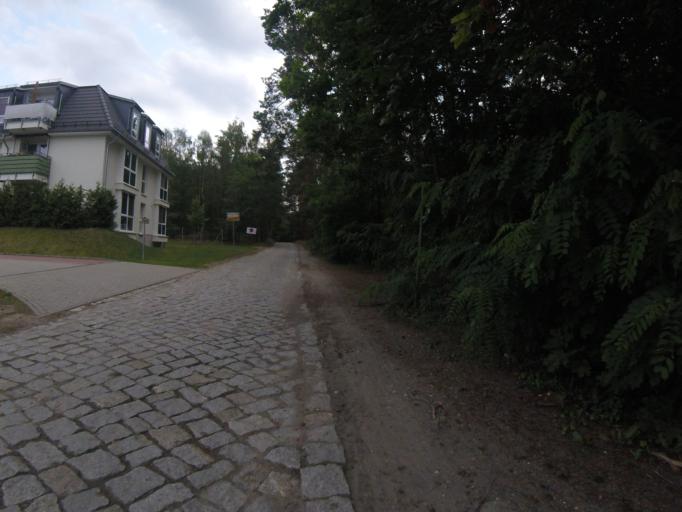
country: DE
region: Brandenburg
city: Schwerin
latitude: 52.1931
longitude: 13.5846
